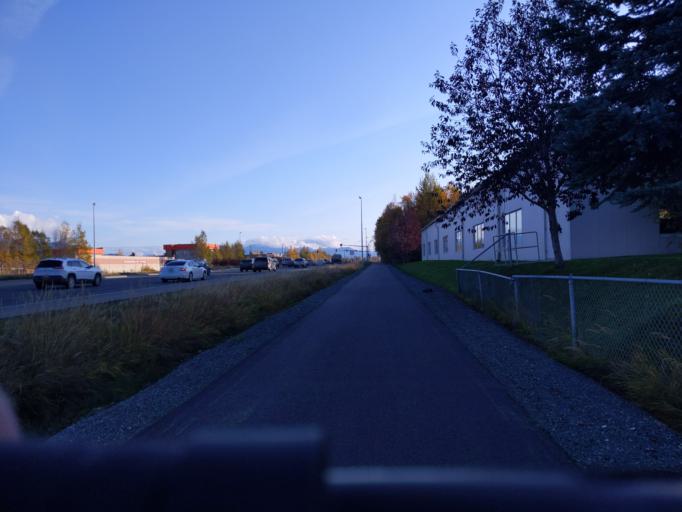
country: US
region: Alaska
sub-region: Anchorage Municipality
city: Anchorage
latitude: 61.1727
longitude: -149.8869
